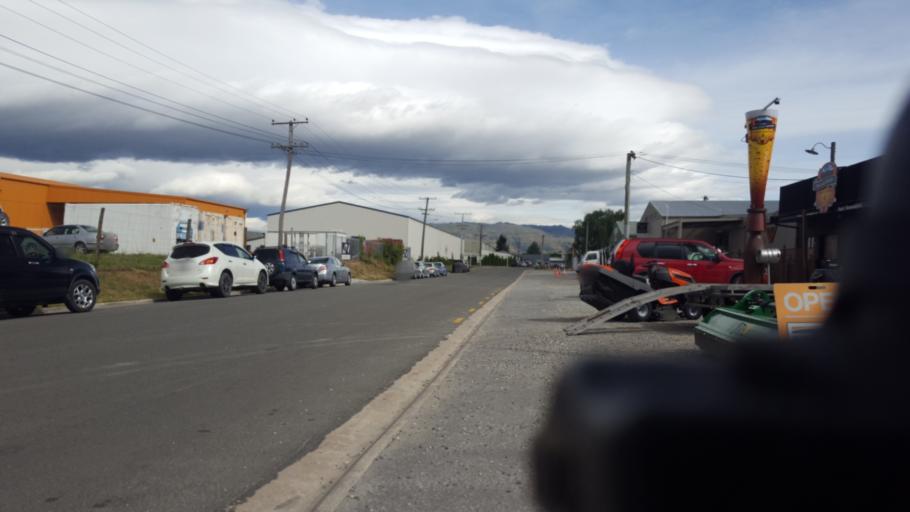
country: NZ
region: Otago
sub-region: Queenstown-Lakes District
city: Wanaka
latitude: -45.2479
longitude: 169.3987
